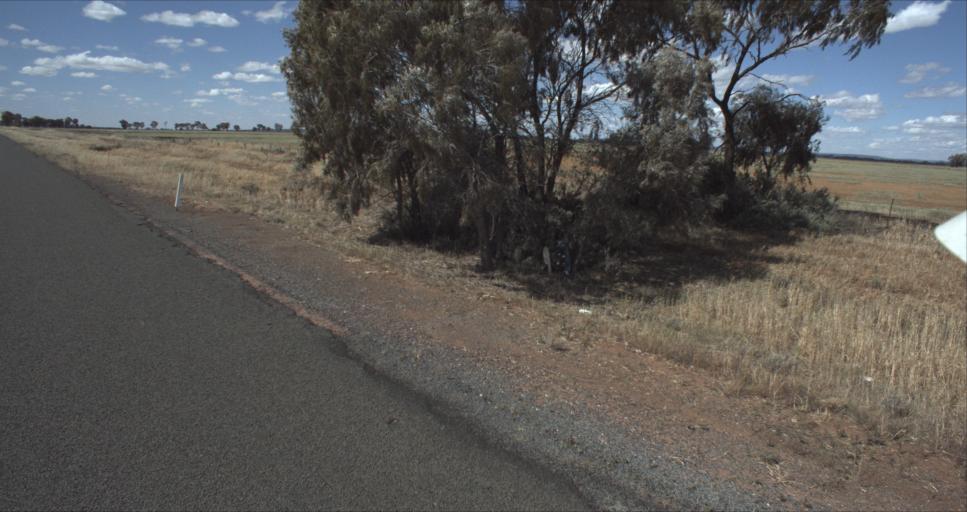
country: AU
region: New South Wales
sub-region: Leeton
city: Leeton
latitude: -34.4683
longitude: 146.2514
